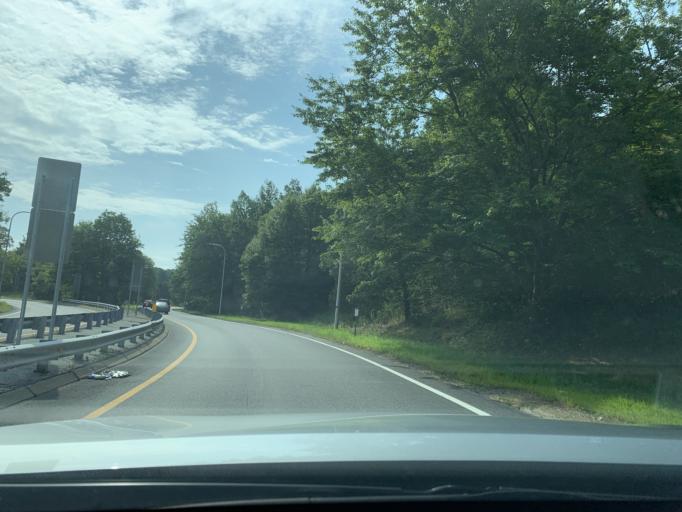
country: US
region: Rhode Island
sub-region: Kent County
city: East Greenwich
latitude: 41.6959
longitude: -71.4787
